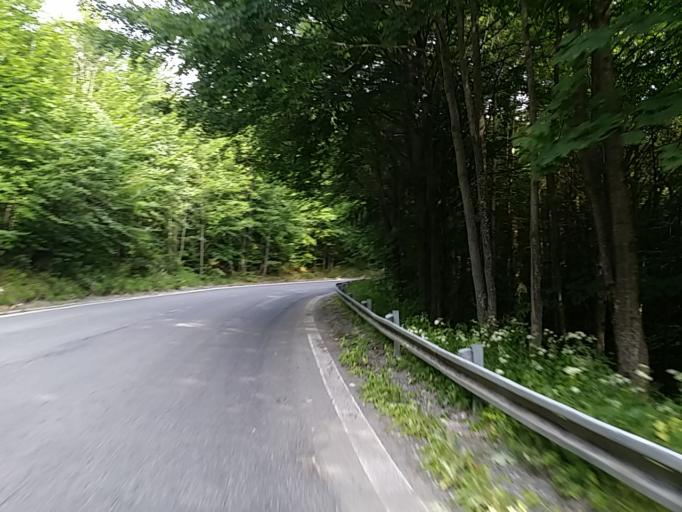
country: SK
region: Kosicky
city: Dobsina
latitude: 48.9026
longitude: 20.2534
